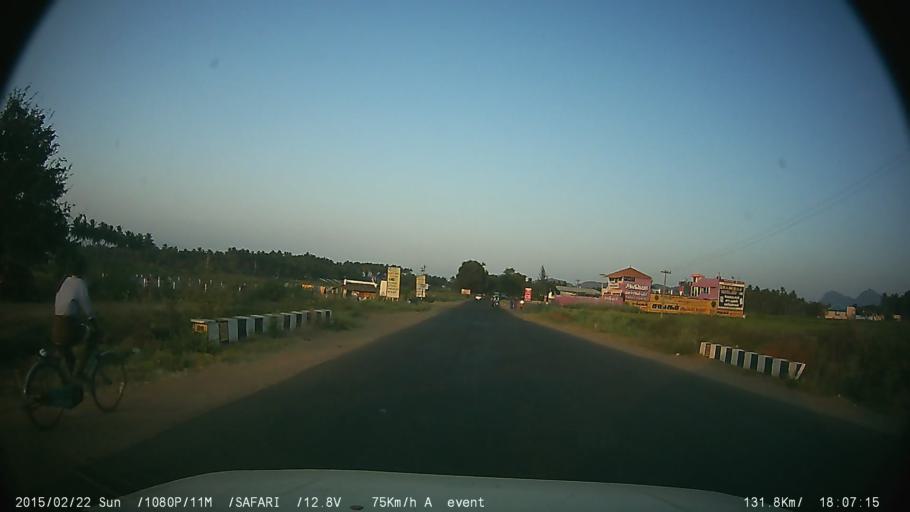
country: IN
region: Tamil Nadu
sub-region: Theni
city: Chinnamanur
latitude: 9.8321
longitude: 77.3733
